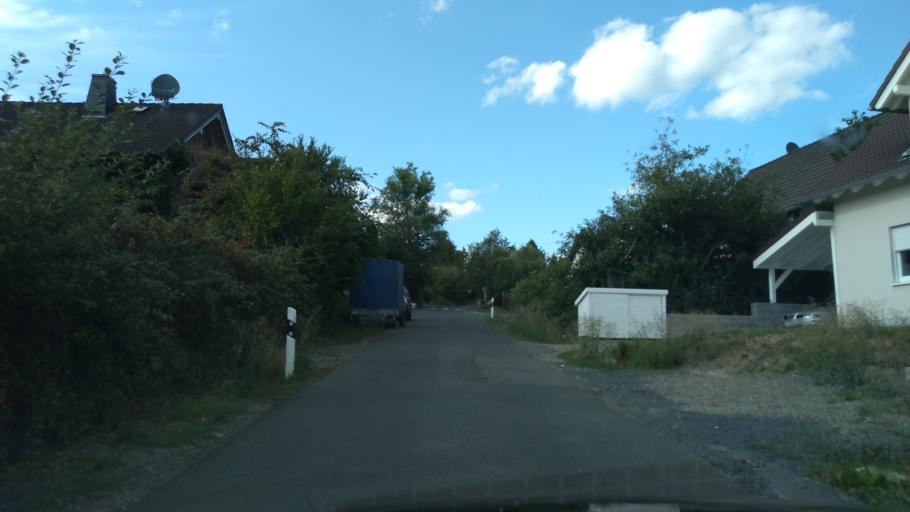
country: DE
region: North Rhine-Westphalia
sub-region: Regierungsbezirk Koln
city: Much
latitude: 50.8751
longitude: 7.3834
